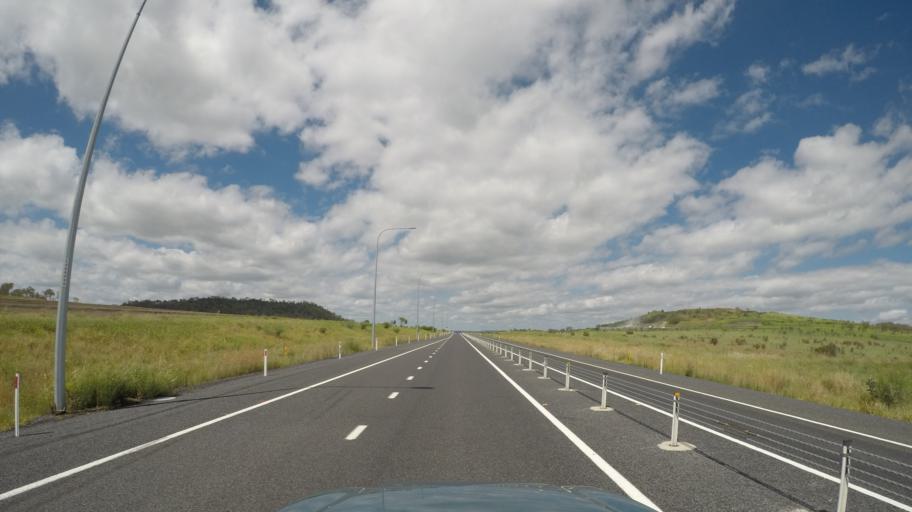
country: AU
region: Queensland
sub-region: Toowoomba
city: Westbrook
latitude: -27.5513
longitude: 151.8285
